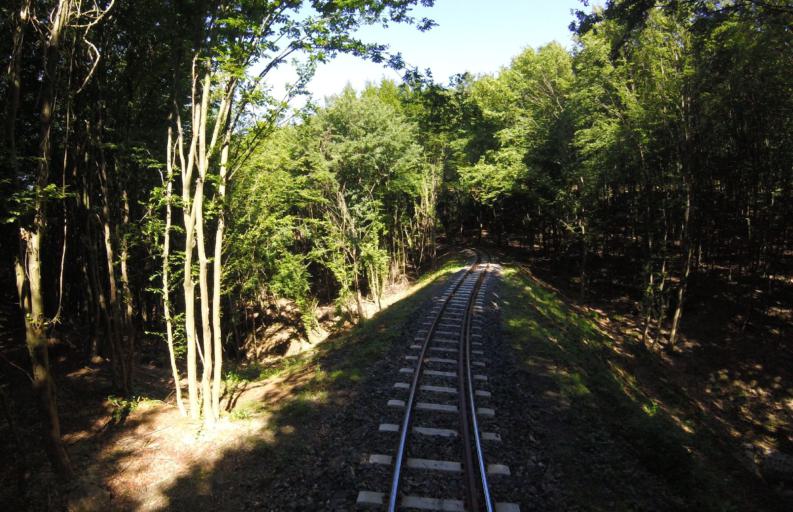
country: HU
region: Pest
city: Szob
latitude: 47.8927
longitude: 18.8797
